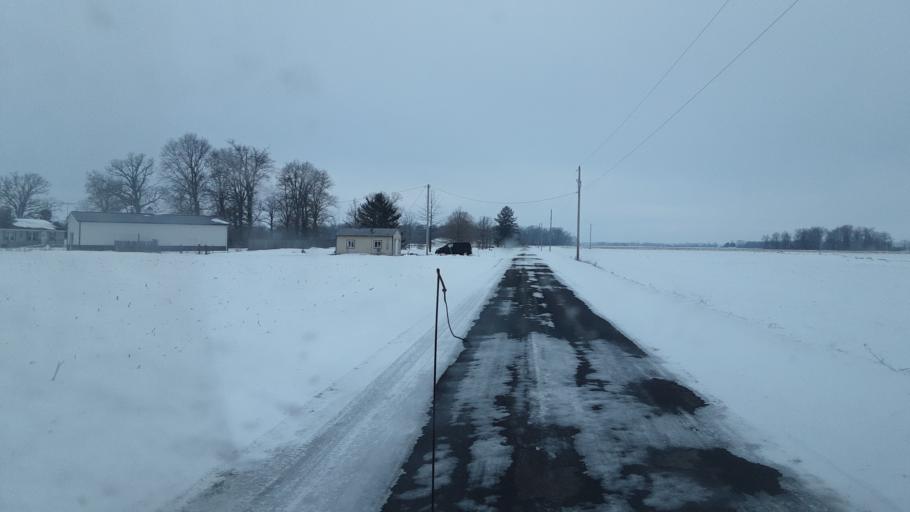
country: US
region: Ohio
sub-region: Union County
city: Marysville
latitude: 40.1268
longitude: -83.4187
